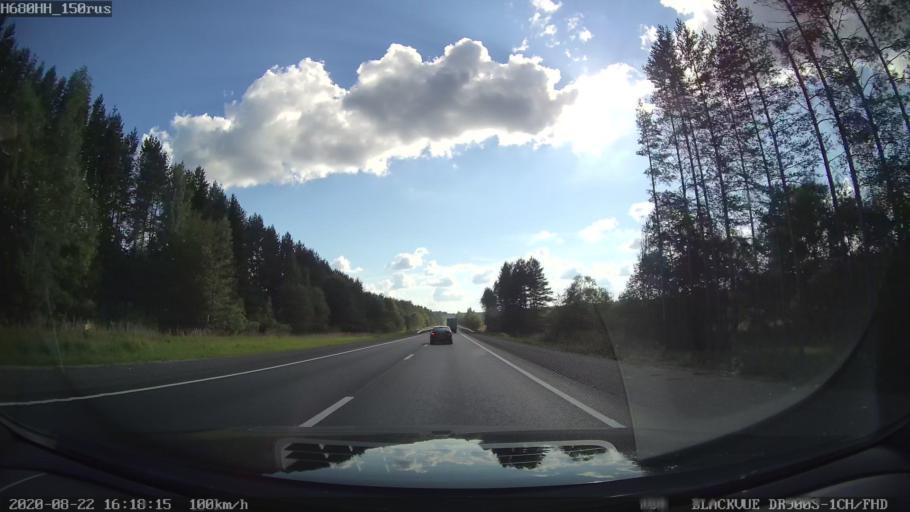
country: RU
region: Tverskaya
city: Rameshki
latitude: 57.4190
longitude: 36.1446
